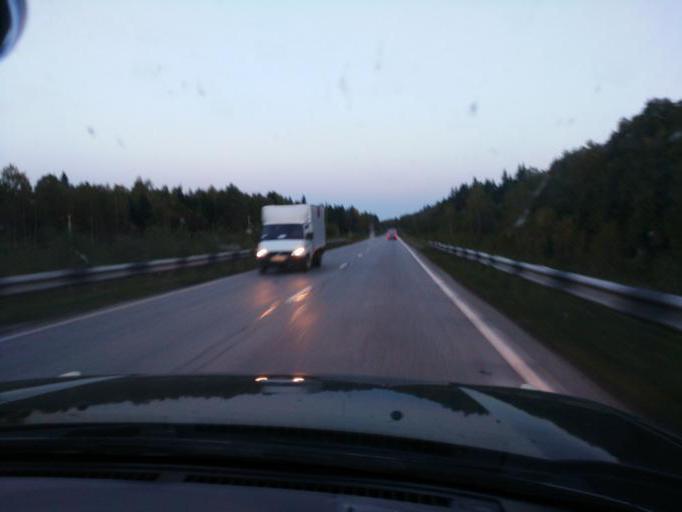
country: RU
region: Perm
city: Verkhnechusovskiye Gorodki
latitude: 58.2518
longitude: 57.0099
